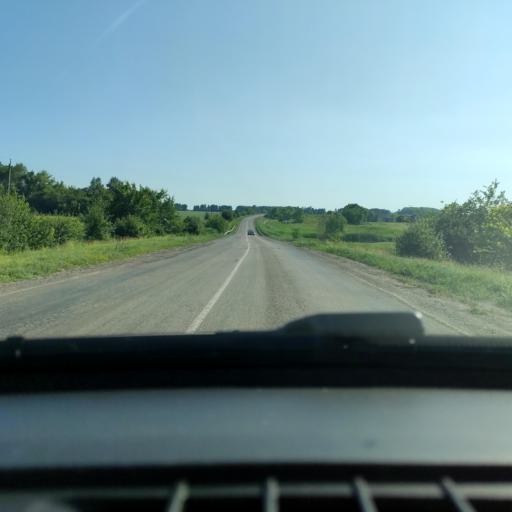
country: RU
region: Voronezj
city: Panino
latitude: 51.6120
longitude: 40.0057
